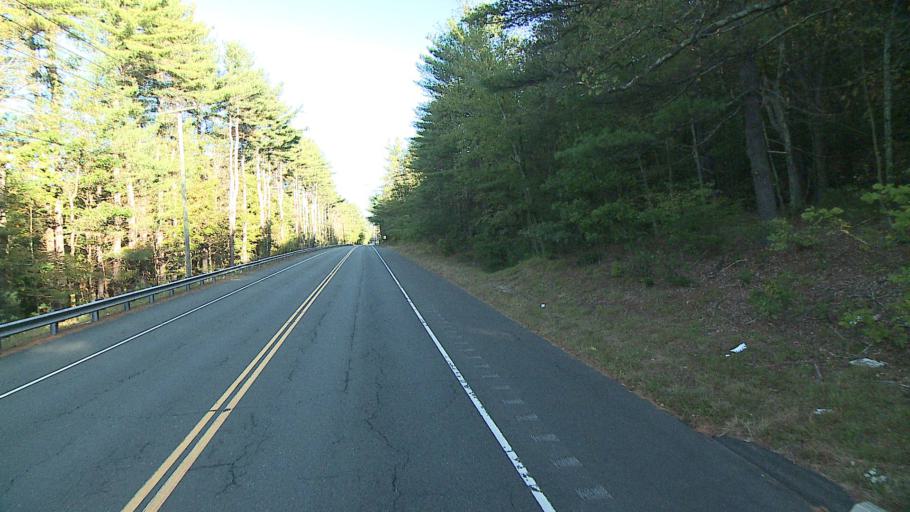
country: US
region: Connecticut
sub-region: Hartford County
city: Collinsville
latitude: 41.8221
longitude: -72.9710
